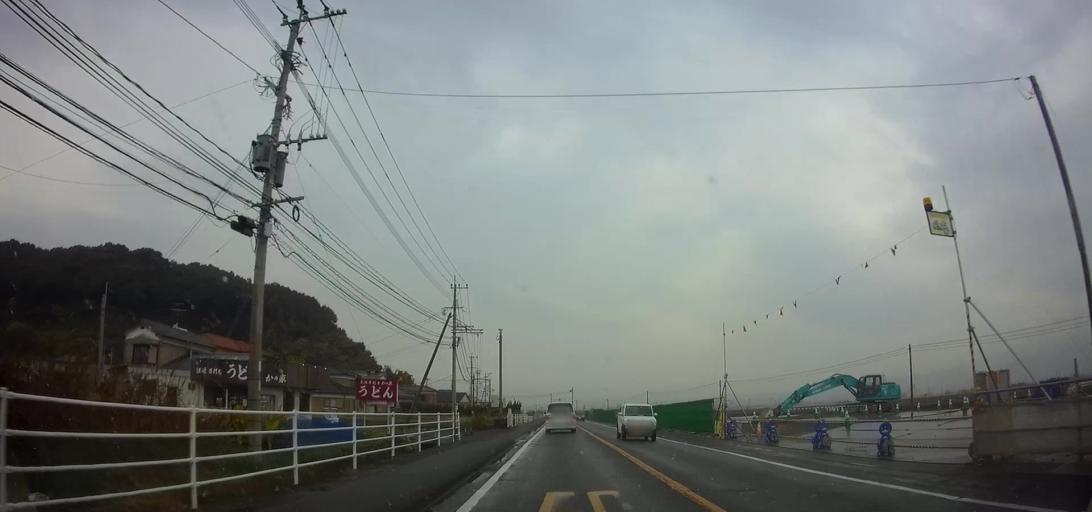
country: JP
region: Nagasaki
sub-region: Isahaya-shi
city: Isahaya
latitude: 32.8368
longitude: 130.1060
